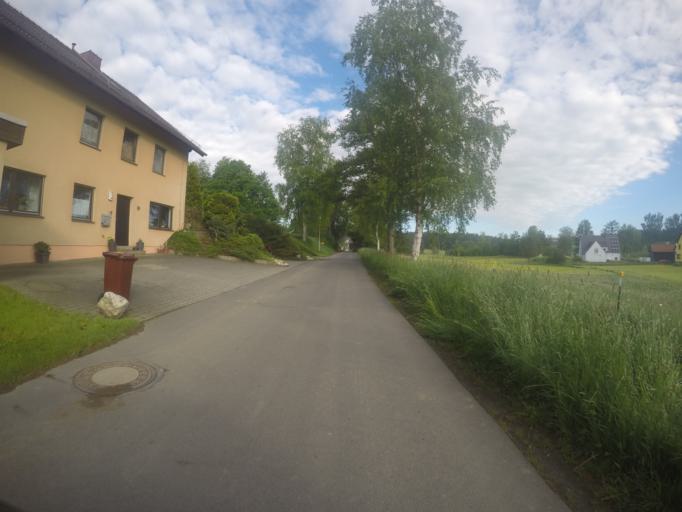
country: DE
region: Bavaria
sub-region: Upper Franconia
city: Schonwald
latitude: 50.2088
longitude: 12.1224
